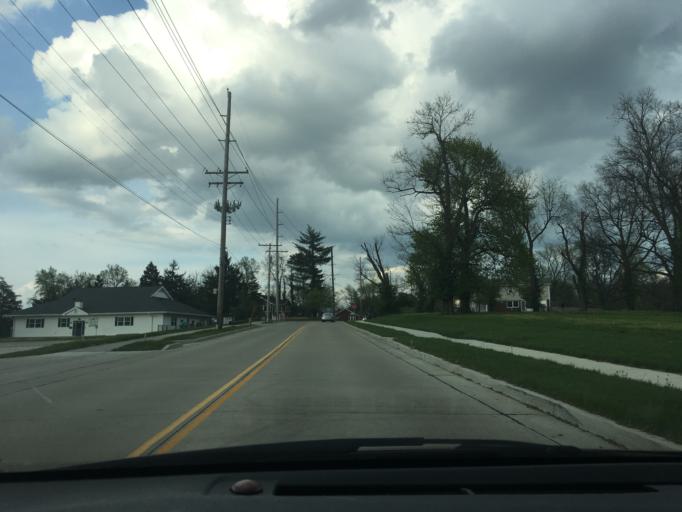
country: US
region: Missouri
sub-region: Saint Louis County
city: Maryland Heights
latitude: 38.7255
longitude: -90.4172
